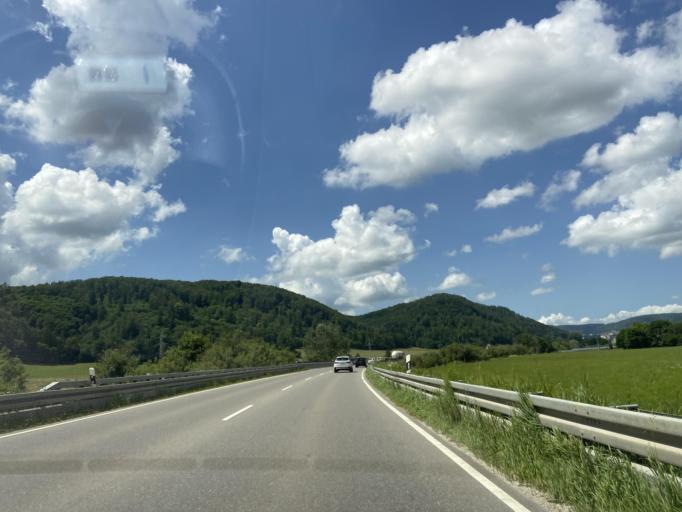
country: DE
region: Baden-Wuerttemberg
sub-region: Tuebingen Region
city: Strassberg
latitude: 48.1919
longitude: 9.0647
